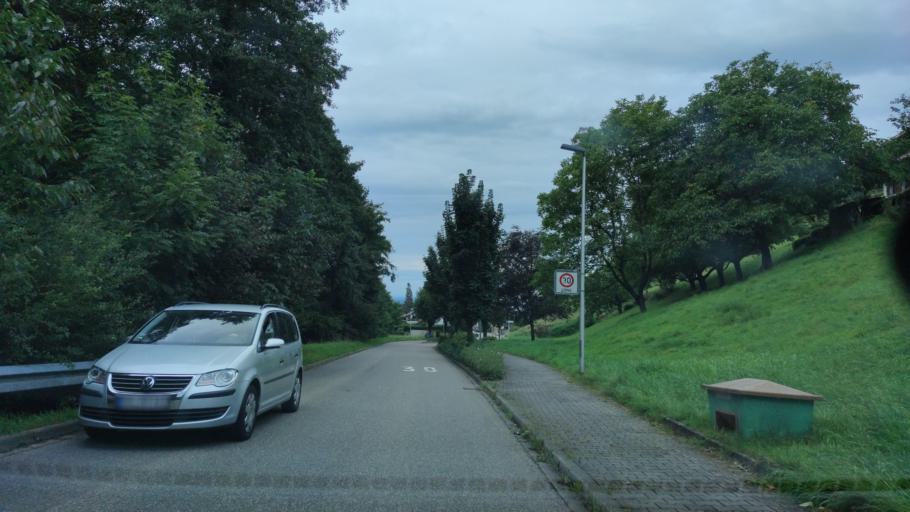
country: DE
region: Baden-Wuerttemberg
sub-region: Freiburg Region
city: Lauf
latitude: 48.6440
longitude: 8.1400
